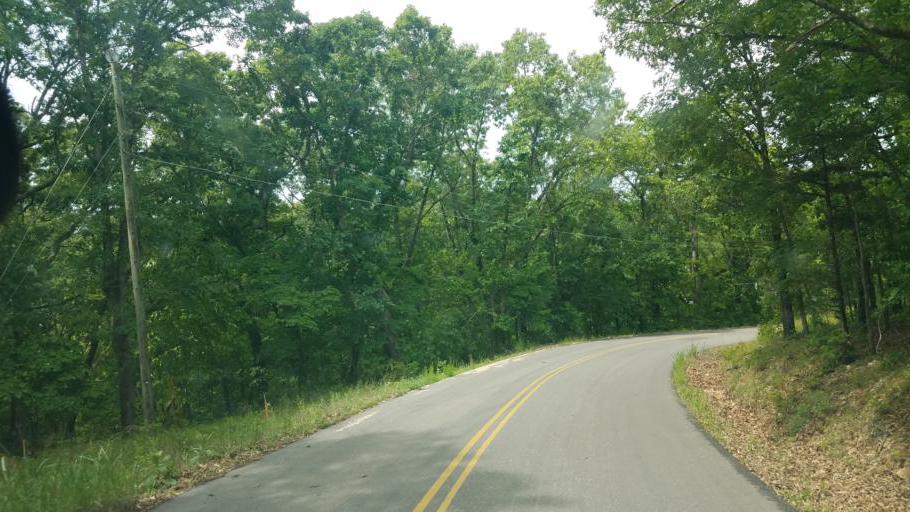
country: US
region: Missouri
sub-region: Camden County
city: Four Seasons
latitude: 38.1650
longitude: -92.6828
